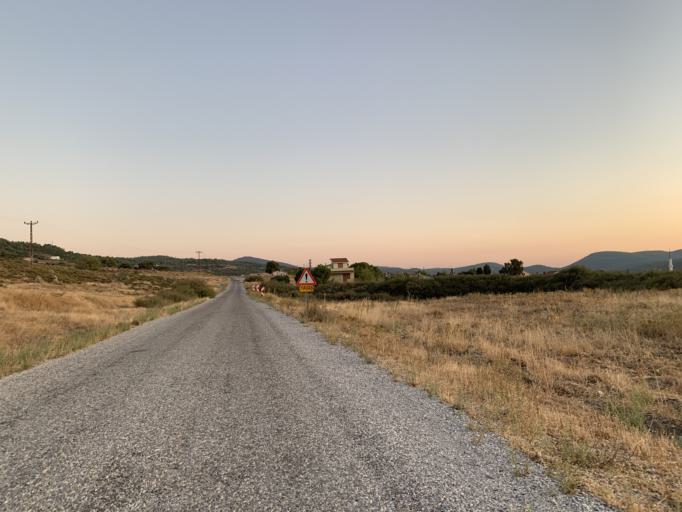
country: TR
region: Izmir
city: Uzunkuyu
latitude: 38.3265
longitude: 26.5837
